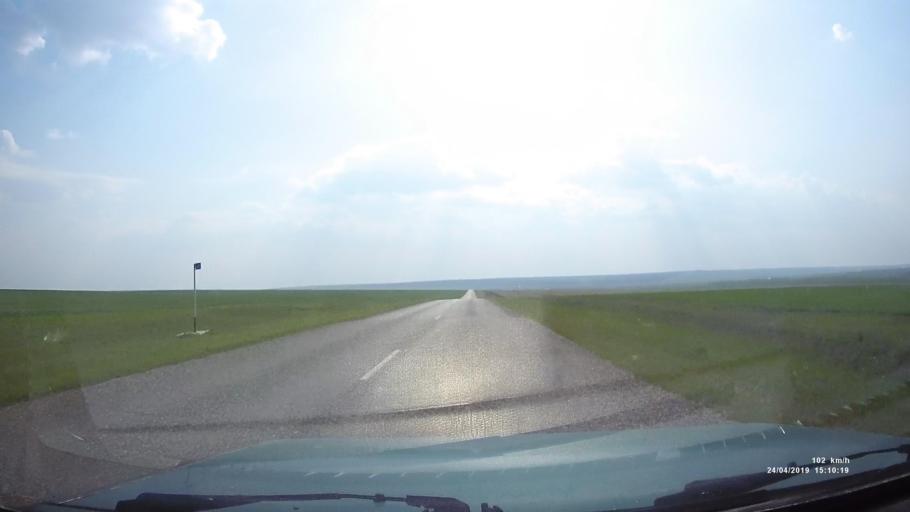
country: RU
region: Rostov
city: Remontnoye
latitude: 46.5507
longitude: 43.3436
